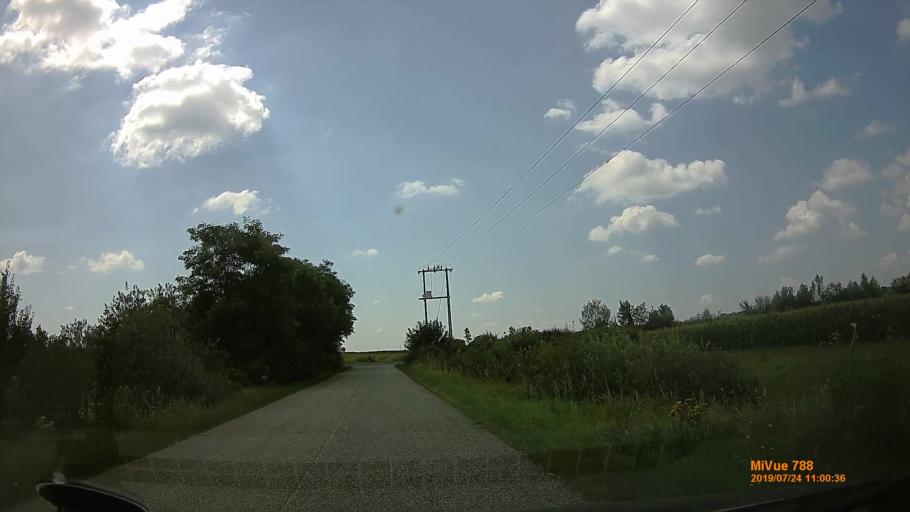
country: HU
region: Szabolcs-Szatmar-Bereg
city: Tarpa
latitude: 48.1610
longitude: 22.5159
